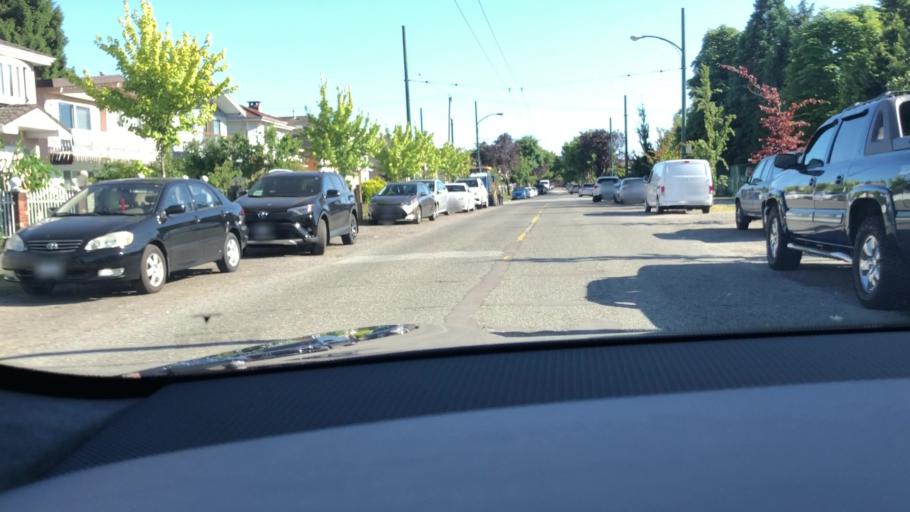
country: CA
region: British Columbia
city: Vancouver
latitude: 49.2314
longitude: -123.0670
